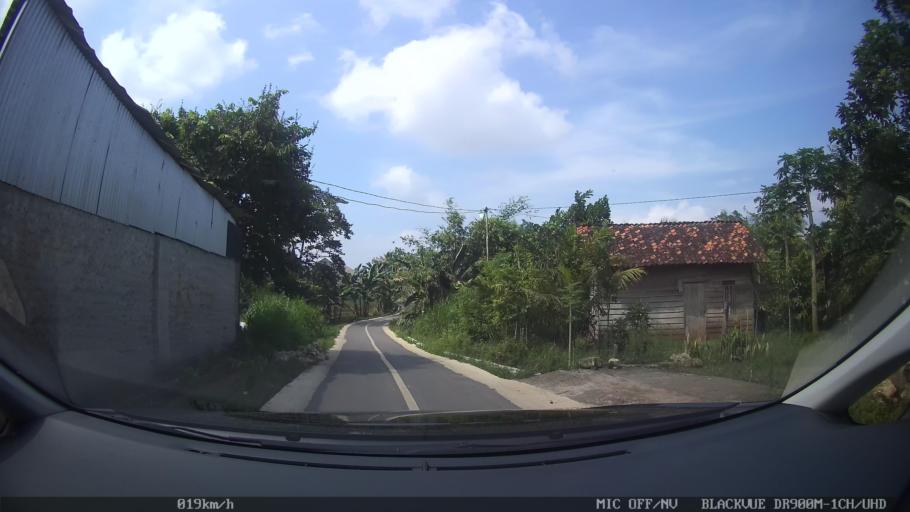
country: ID
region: Lampung
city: Kedaton
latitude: -5.3379
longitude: 105.2725
